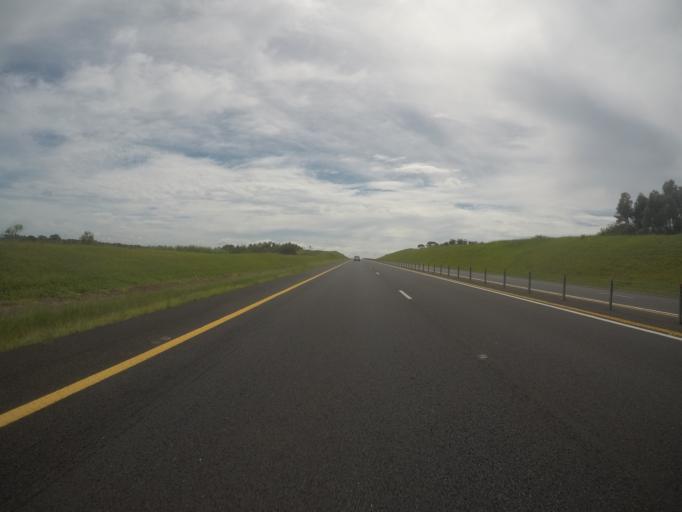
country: ZA
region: KwaZulu-Natal
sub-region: iLembe District Municipality
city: Mandeni
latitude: -29.0649
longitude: 31.6237
